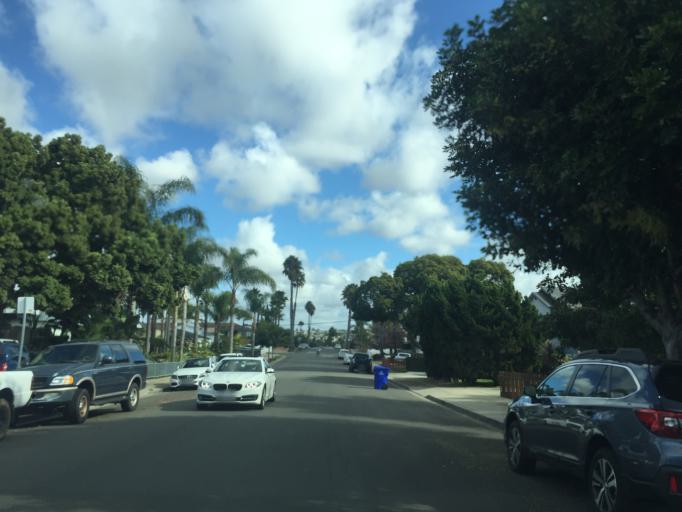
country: US
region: California
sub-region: San Diego County
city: La Jolla
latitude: 32.7986
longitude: -117.2321
